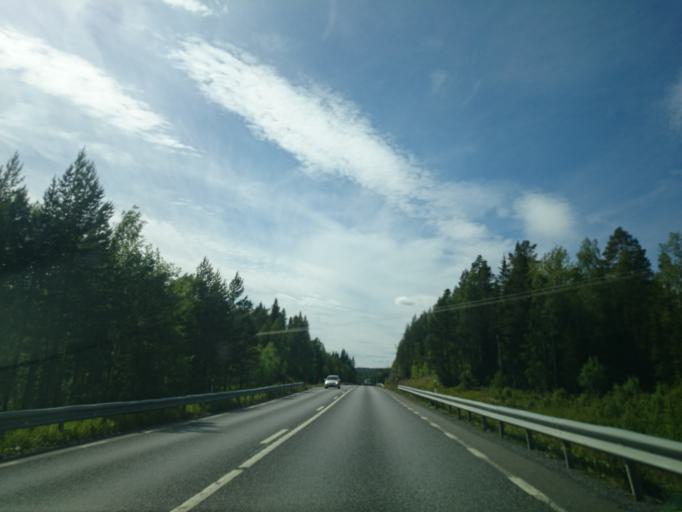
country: SE
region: Jaemtland
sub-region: Krokoms Kommun
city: Valla
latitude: 63.3371
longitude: 14.0011
